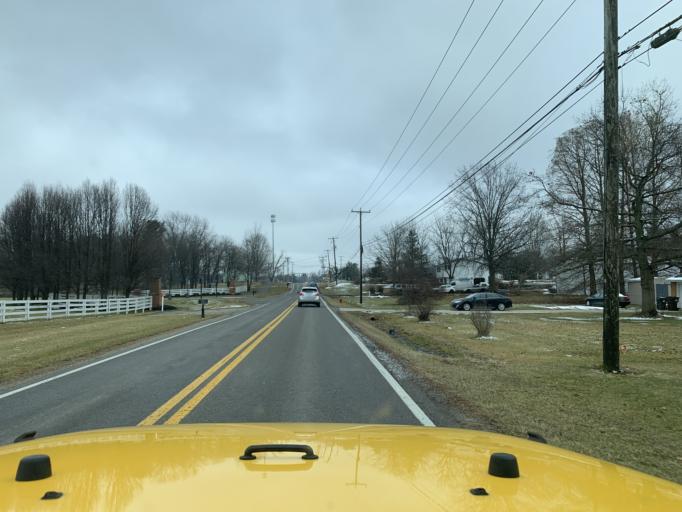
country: US
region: Ohio
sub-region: Franklin County
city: New Albany
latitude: 40.0967
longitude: -82.7848
